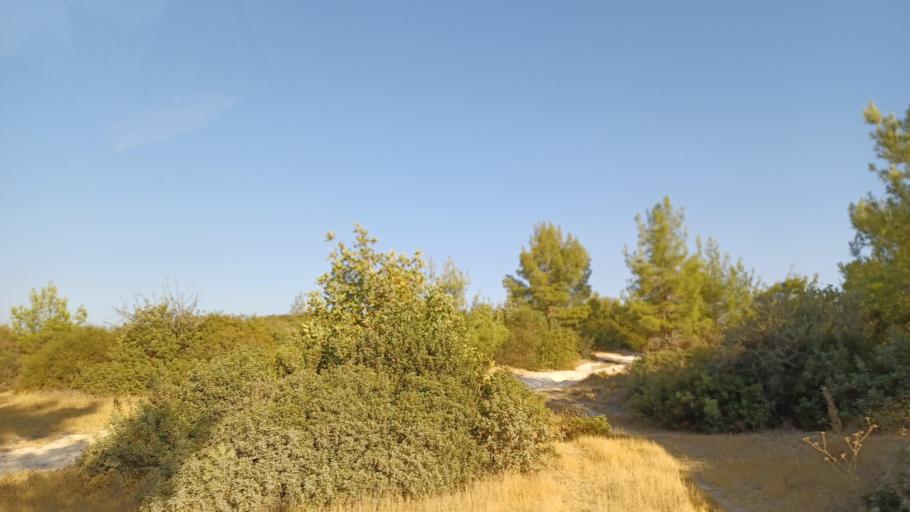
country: CY
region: Limassol
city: Pissouri
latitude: 34.7257
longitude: 32.6796
